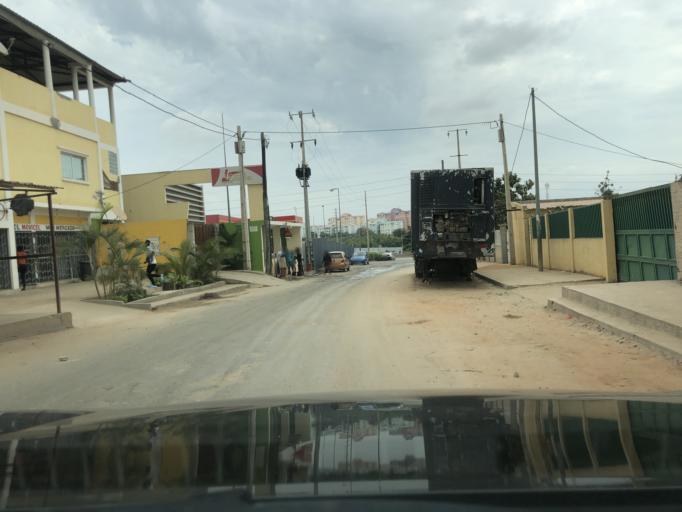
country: AO
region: Luanda
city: Luanda
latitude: -8.9204
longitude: 13.2253
